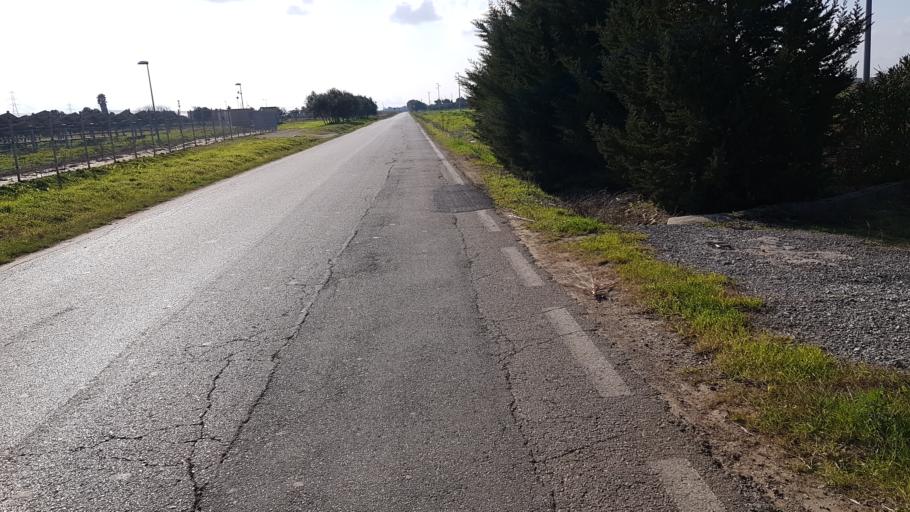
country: IT
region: Apulia
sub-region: Provincia di Brindisi
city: La Rosa
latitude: 40.5844
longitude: 17.9025
